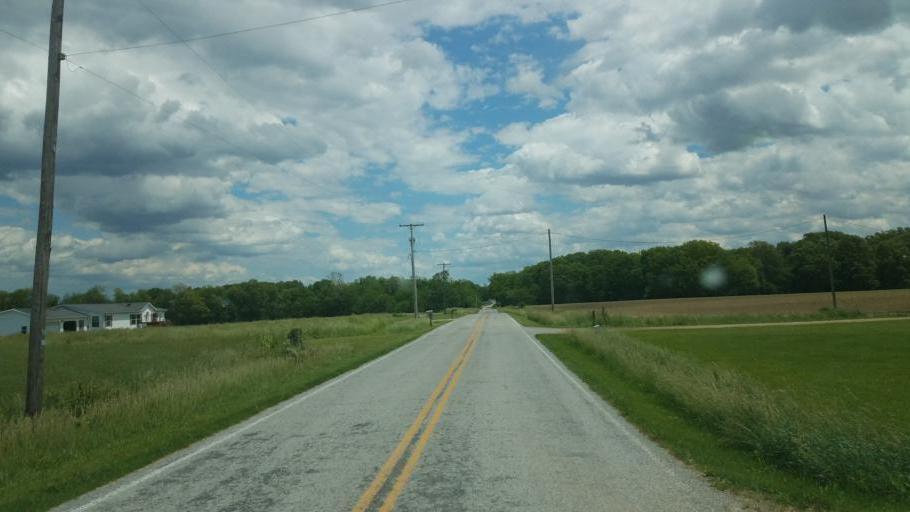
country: US
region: Ohio
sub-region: Huron County
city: Monroeville
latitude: 41.1850
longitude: -82.7320
